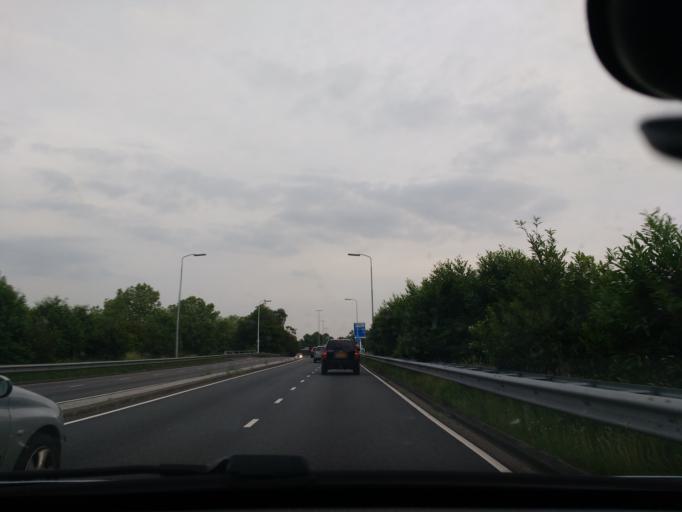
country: NL
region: North Brabant
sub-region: Gemeente Eindhoven
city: Lakerlopen
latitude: 51.4341
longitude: 5.5037
